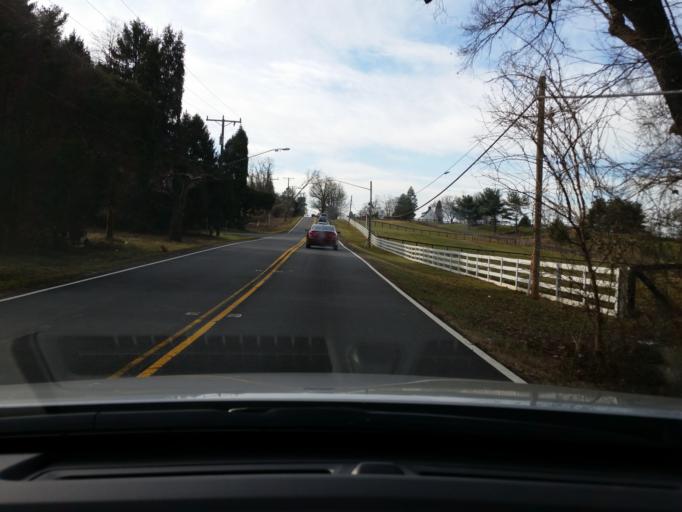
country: US
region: Virginia
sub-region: Fairfax County
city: Tysons Corner
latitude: 38.9634
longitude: -77.2300
